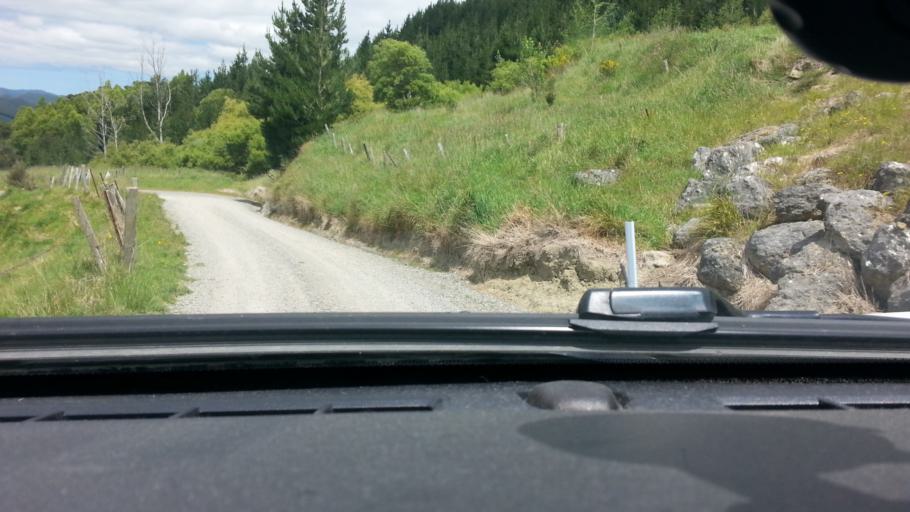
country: NZ
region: Wellington
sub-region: Masterton District
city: Masterton
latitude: -41.1600
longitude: 175.6787
